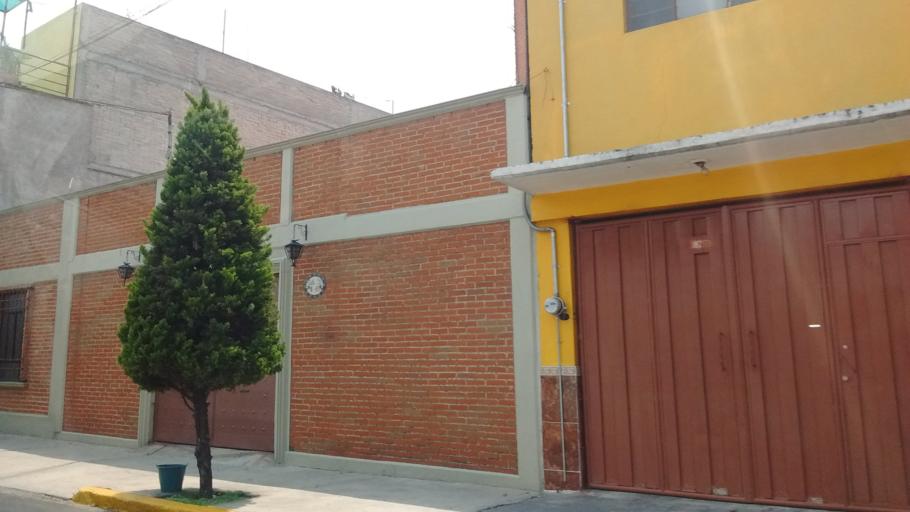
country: MX
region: Mexico City
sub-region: Iztacalco
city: Iztacalco
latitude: 19.4107
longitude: -99.0920
